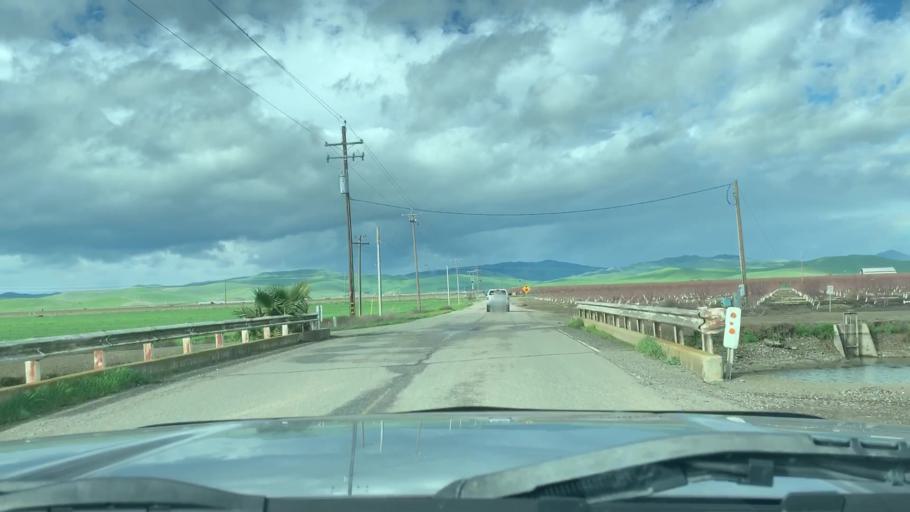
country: US
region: California
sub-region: Merced County
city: Gustine
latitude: 37.1225
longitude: -121.0123
